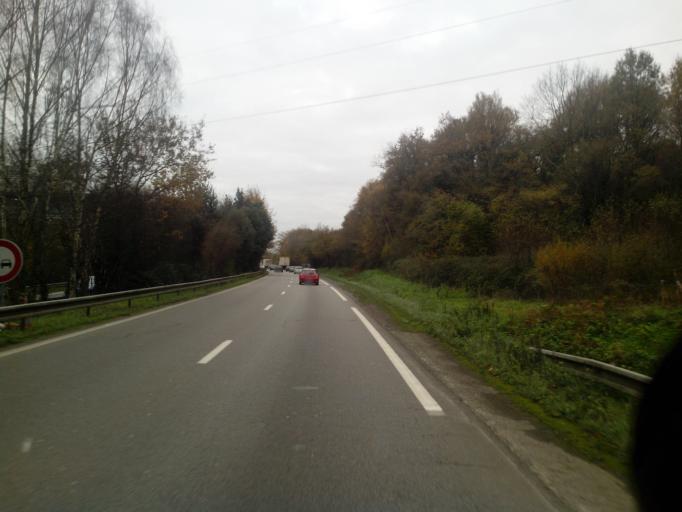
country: FR
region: Pays de la Loire
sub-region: Departement de la Loire-Atlantique
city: La Chapelle-sur-Erdre
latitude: 47.2659
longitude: -1.5602
